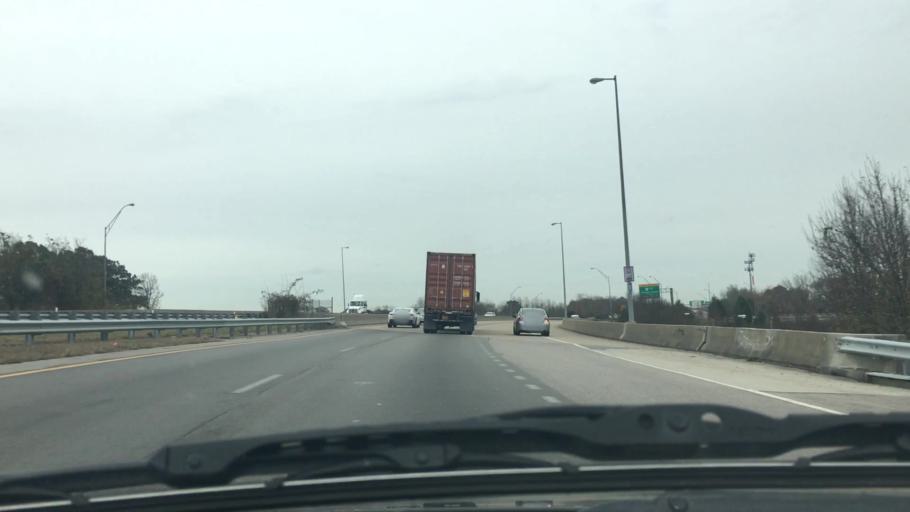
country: US
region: Virginia
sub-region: City of Portsmouth
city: Portsmouth Heights
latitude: 36.8655
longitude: -76.3530
